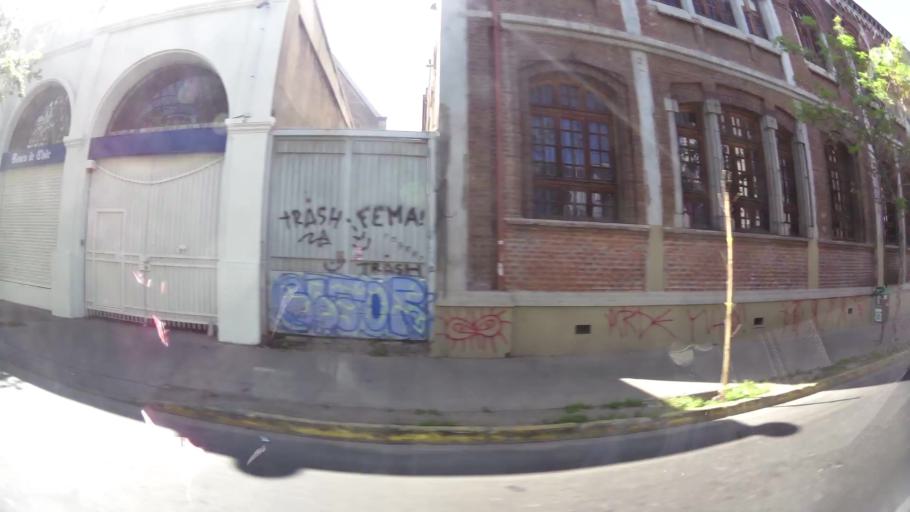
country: CL
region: Santiago Metropolitan
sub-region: Provincia de Santiago
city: Santiago
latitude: -33.4479
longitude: -70.6647
